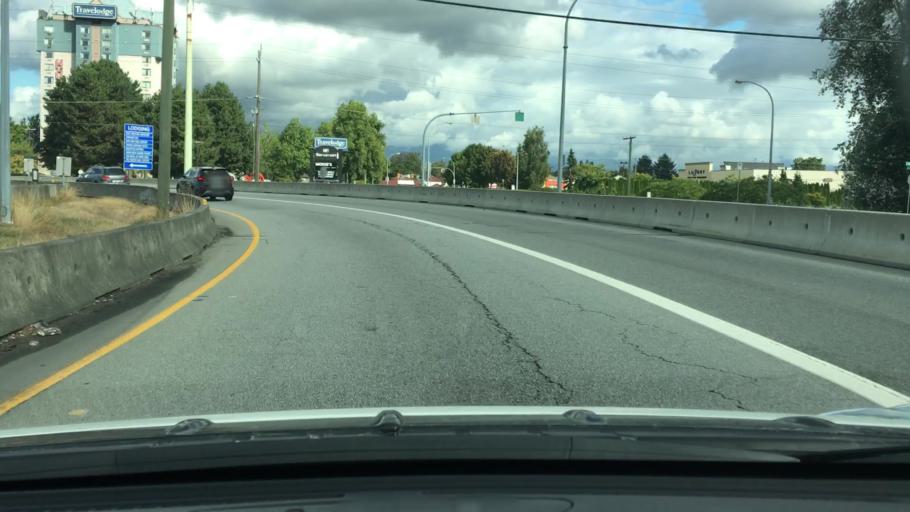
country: CA
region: British Columbia
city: Richmond
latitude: 49.1896
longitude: -123.1126
